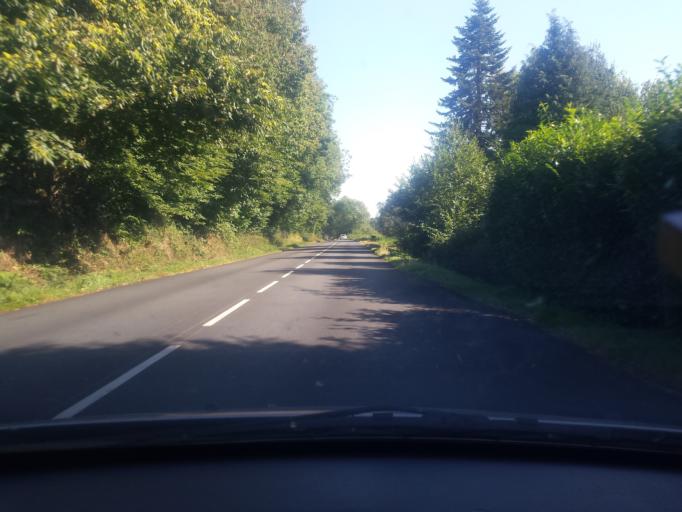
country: FR
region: Brittany
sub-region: Departement du Morbihan
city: Malguenac
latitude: 48.0926
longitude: -3.0162
